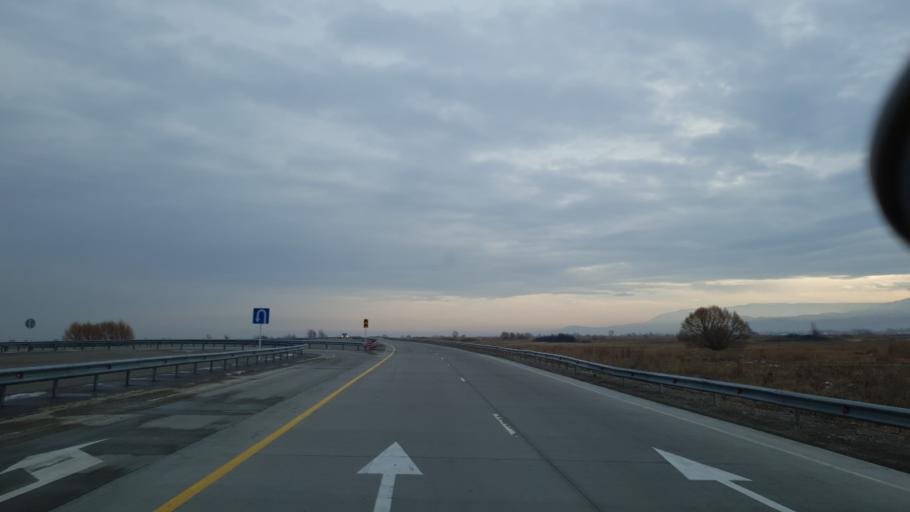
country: KZ
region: Almaty Oblysy
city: Turgen'
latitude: 43.5309
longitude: 77.6024
